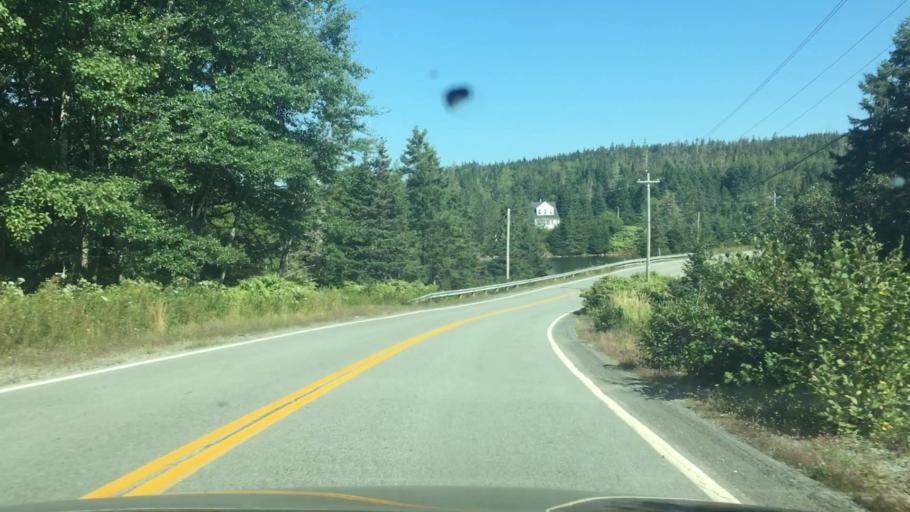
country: CA
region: Nova Scotia
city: New Glasgow
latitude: 44.8209
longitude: -62.6346
